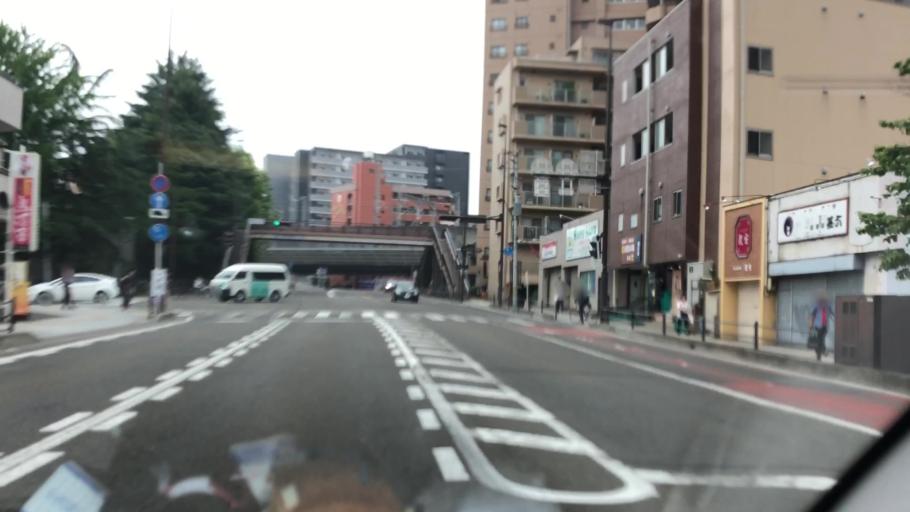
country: JP
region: Miyagi
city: Sendai-shi
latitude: 38.2655
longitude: 140.8828
